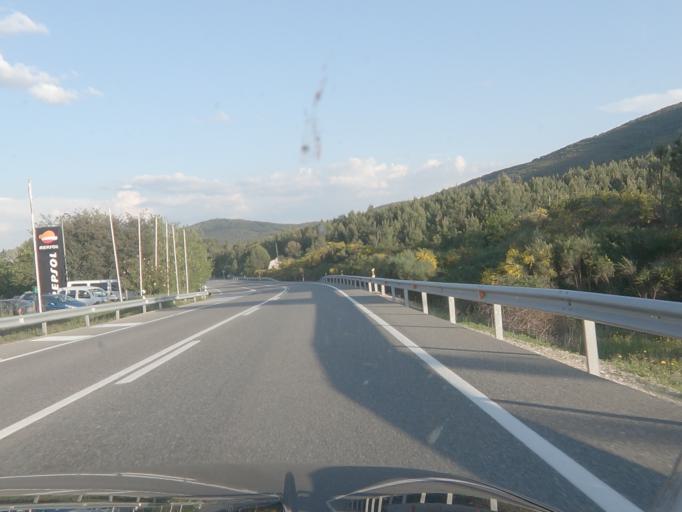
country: PT
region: Portalegre
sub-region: Portalegre
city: Sao Juliao
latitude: 39.3465
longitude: -7.2990
